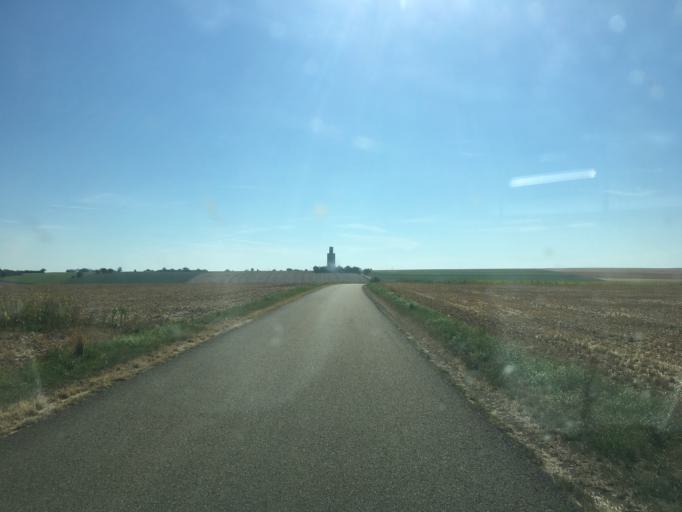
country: FR
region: Bourgogne
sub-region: Departement de l'Yonne
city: Fleury-la-Vallee
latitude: 47.9173
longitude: 3.4135
